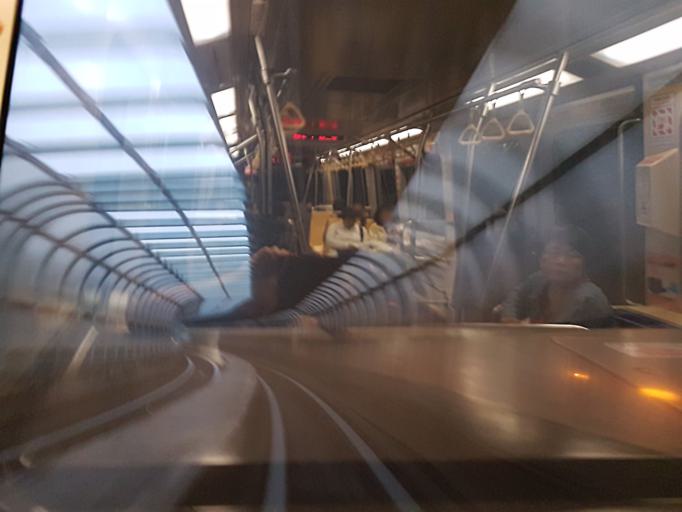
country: TW
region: Taipei
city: Taipei
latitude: 25.0755
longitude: 121.6072
